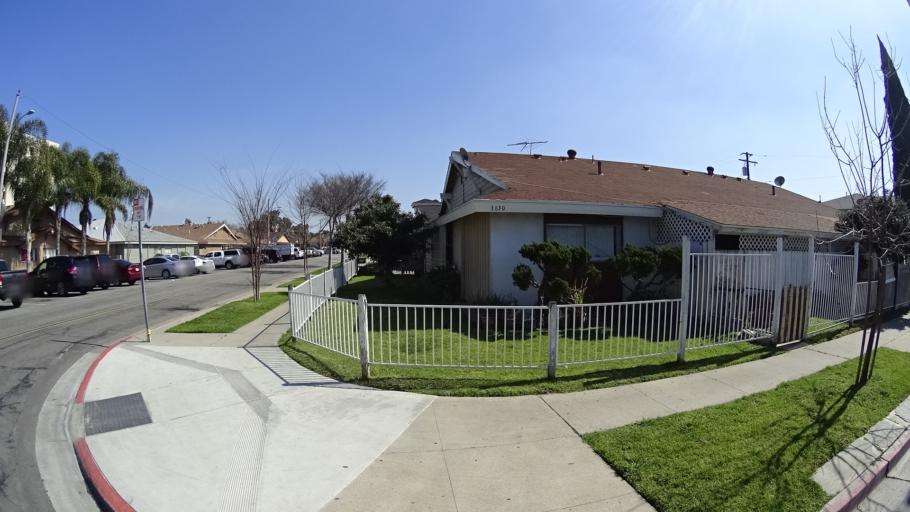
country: US
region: California
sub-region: Orange County
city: Fullerton
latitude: 33.8487
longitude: -117.9466
